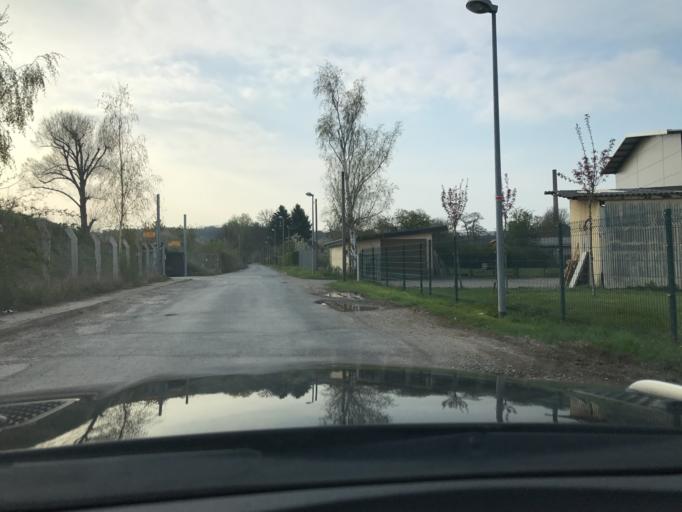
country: DE
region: Thuringia
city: Muehlhausen
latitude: 51.2096
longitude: 10.4783
